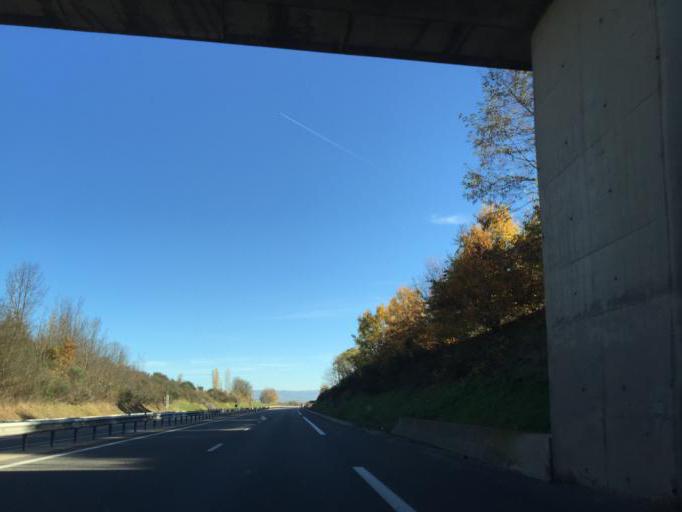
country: FR
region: Rhone-Alpes
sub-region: Departement de la Loire
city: Montrond-les-Bains
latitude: 45.6538
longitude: 4.1729
